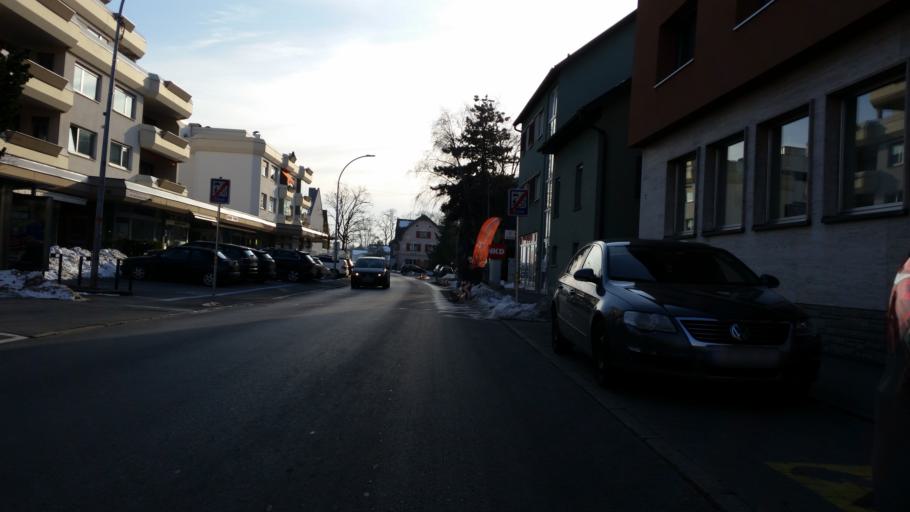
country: AT
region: Vorarlberg
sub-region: Politischer Bezirk Bregenz
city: Hard
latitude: 47.4884
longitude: 9.6885
